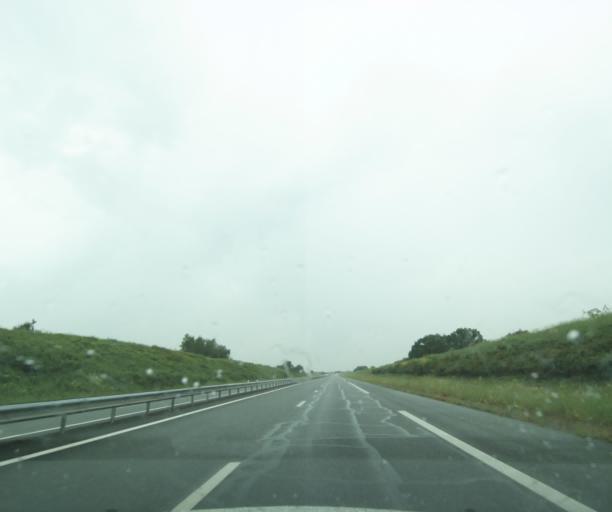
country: FR
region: Auvergne
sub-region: Departement de l'Allier
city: Vallon-en-Sully
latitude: 46.5723
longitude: 2.5346
